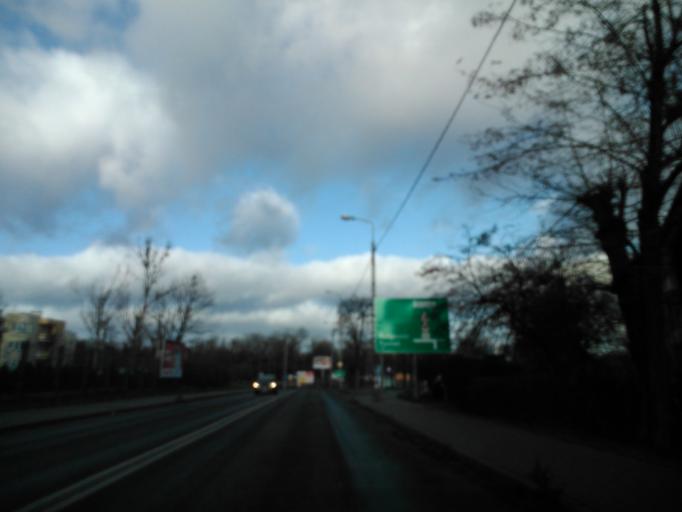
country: PL
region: Kujawsko-Pomorskie
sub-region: Torun
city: Torun
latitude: 52.9996
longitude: 18.6218
